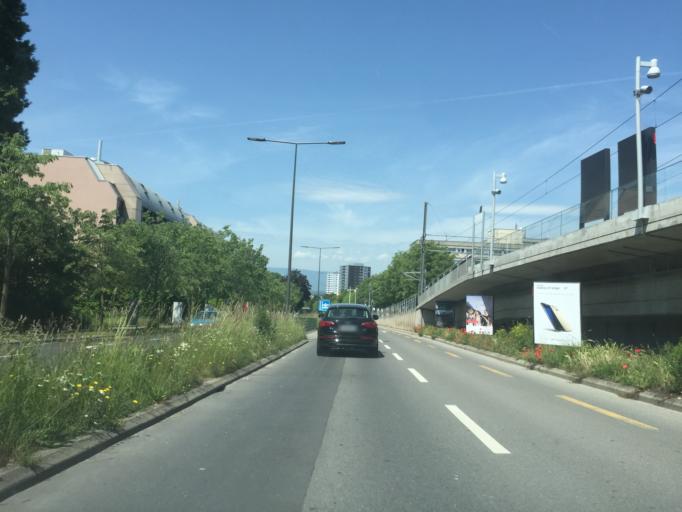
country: CH
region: Vaud
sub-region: Lausanne District
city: Blecherette
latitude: 46.5218
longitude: 6.6133
